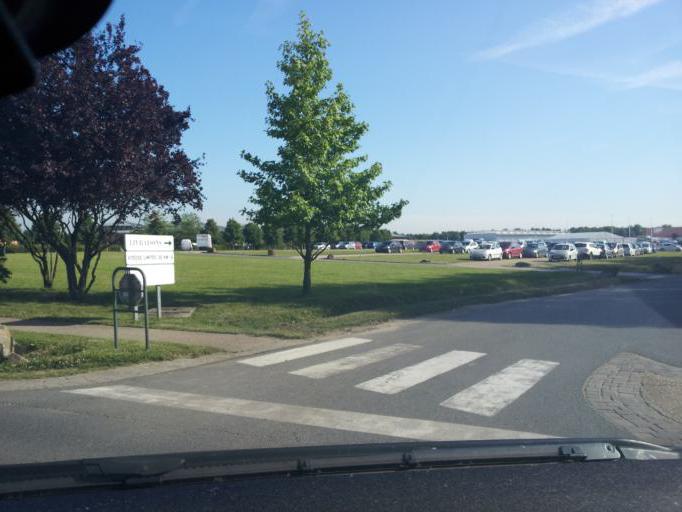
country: FR
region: Ile-de-France
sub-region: Departement de l'Essonne
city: Bondoufle
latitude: 48.5956
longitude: 2.3673
